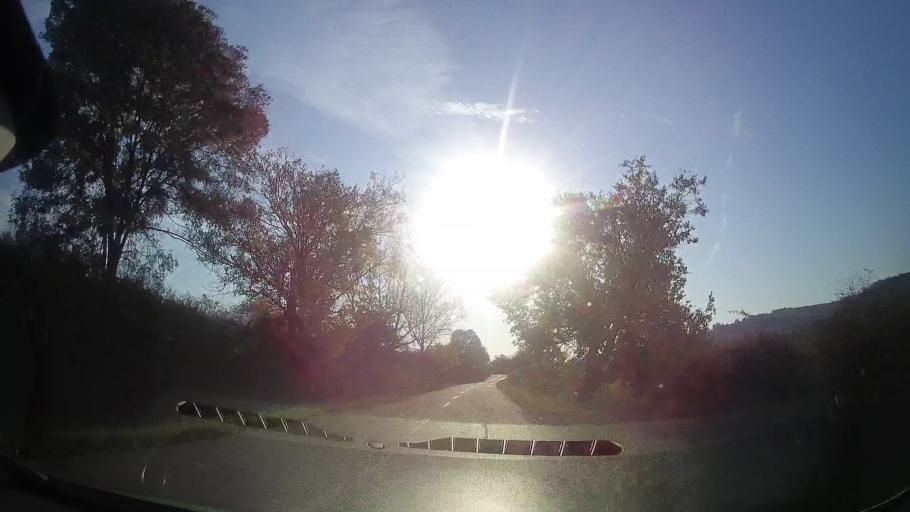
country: RO
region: Timis
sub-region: Comuna Bogda
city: Bogda
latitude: 45.9765
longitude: 21.5848
